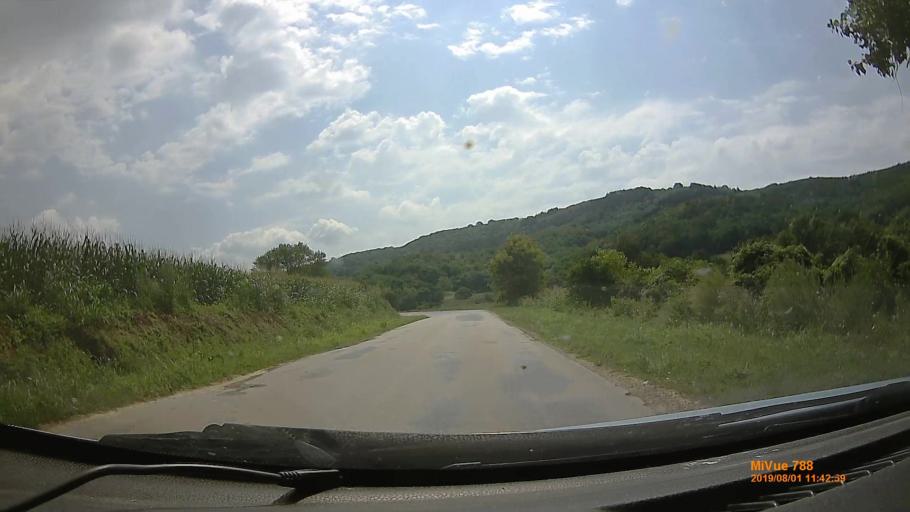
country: HU
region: Baranya
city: Villany
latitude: 45.8821
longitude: 18.4151
